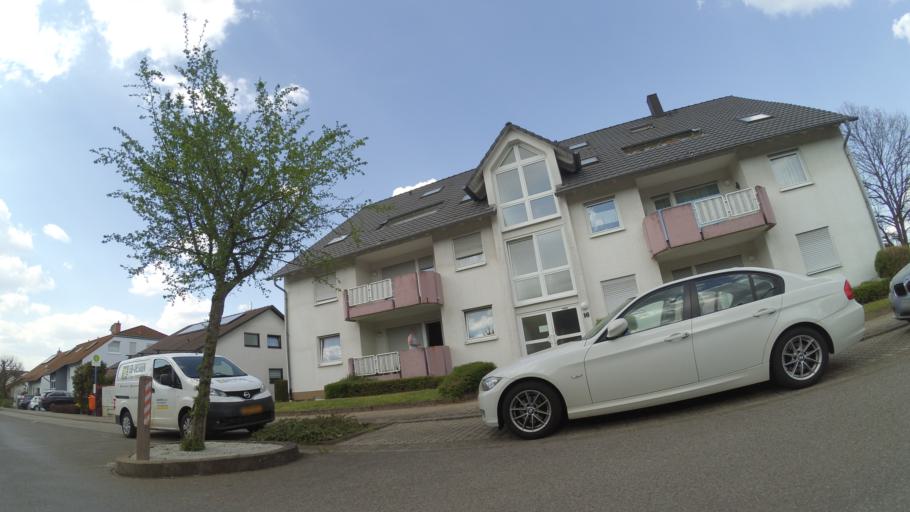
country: DE
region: Saarland
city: Riegelsberg
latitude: 49.3081
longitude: 6.9358
